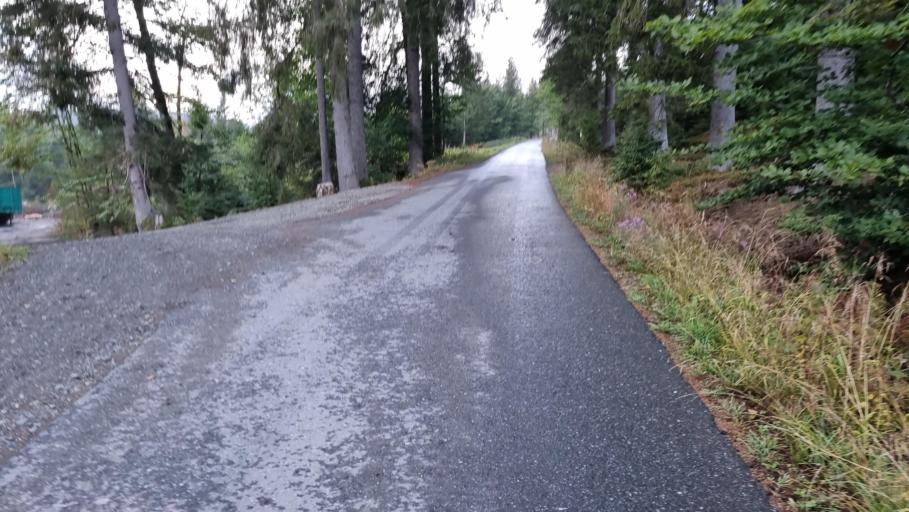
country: DE
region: Lower Saxony
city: Braunlage
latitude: 51.7416
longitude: 10.6094
